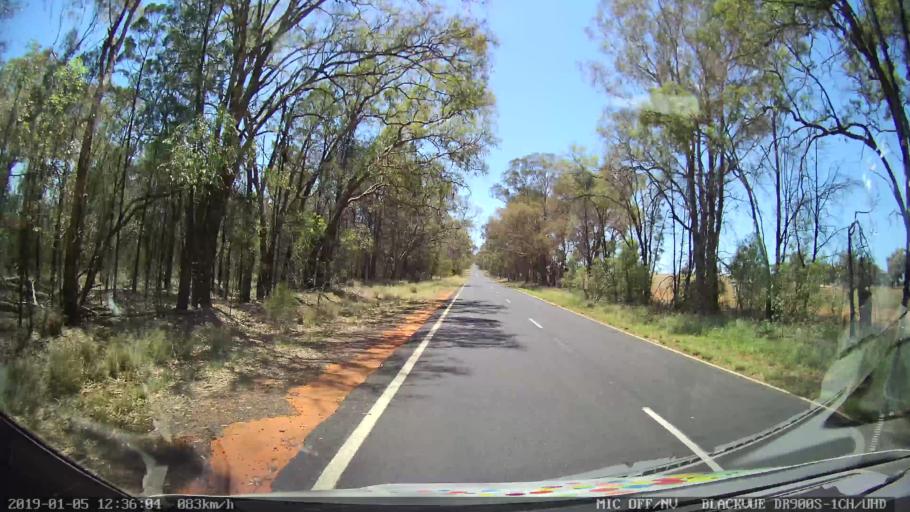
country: AU
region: New South Wales
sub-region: Warrumbungle Shire
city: Coonabarabran
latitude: -31.2081
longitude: 149.4348
